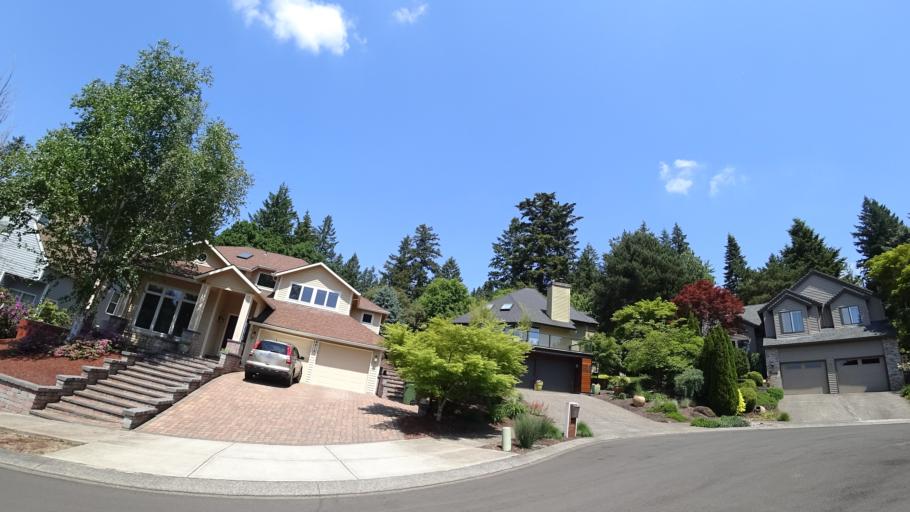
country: US
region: Oregon
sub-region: Washington County
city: Metzger
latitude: 45.4326
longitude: -122.7264
